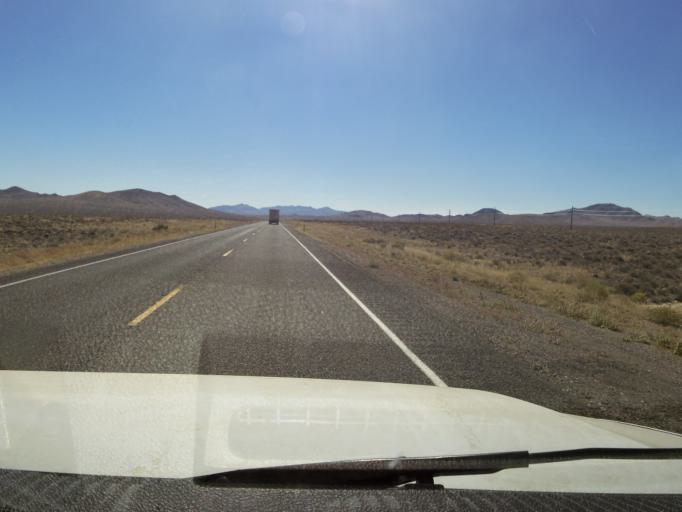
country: US
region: Nevada
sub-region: Nye County
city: Beatty
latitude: 37.0762
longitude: -116.7850
